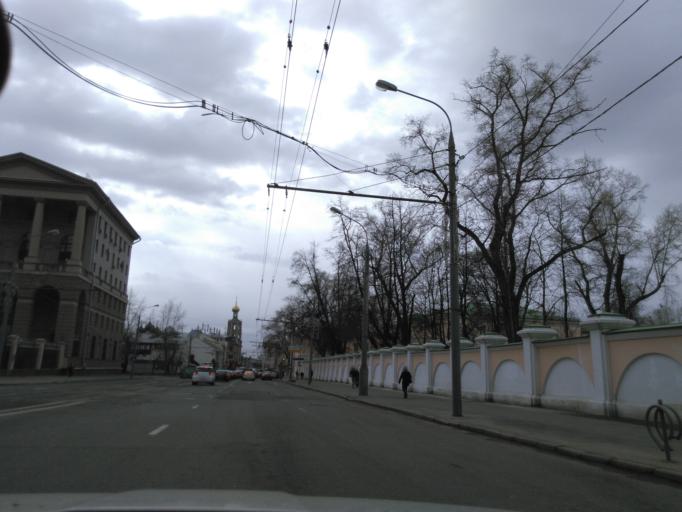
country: RU
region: Moscow
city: Moscow
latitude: 55.7701
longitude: 37.6118
